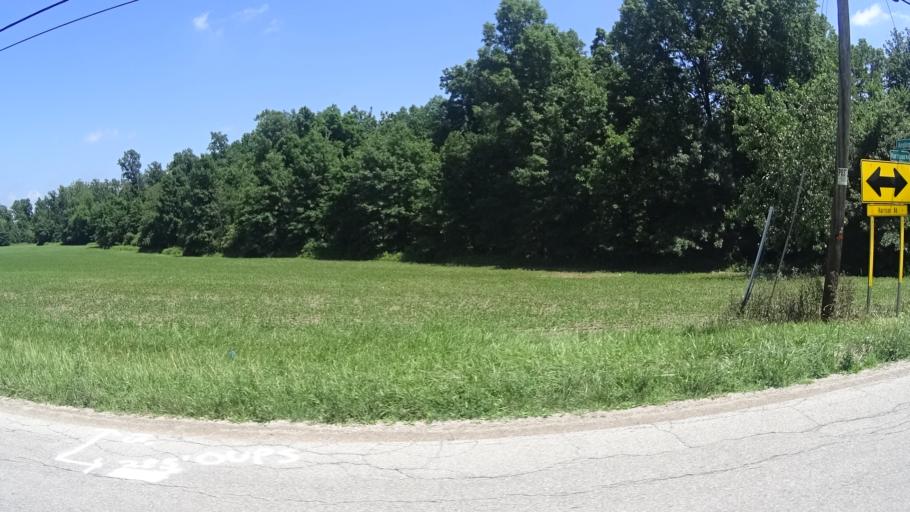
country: US
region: Ohio
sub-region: Lorain County
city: Vermilion
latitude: 41.3542
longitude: -82.3943
